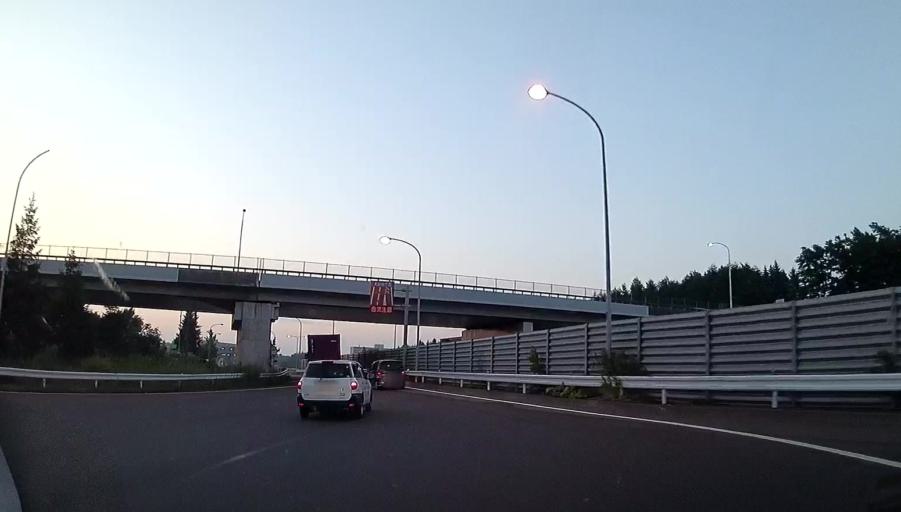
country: JP
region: Hokkaido
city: Kitahiroshima
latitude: 43.0162
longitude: 141.4634
